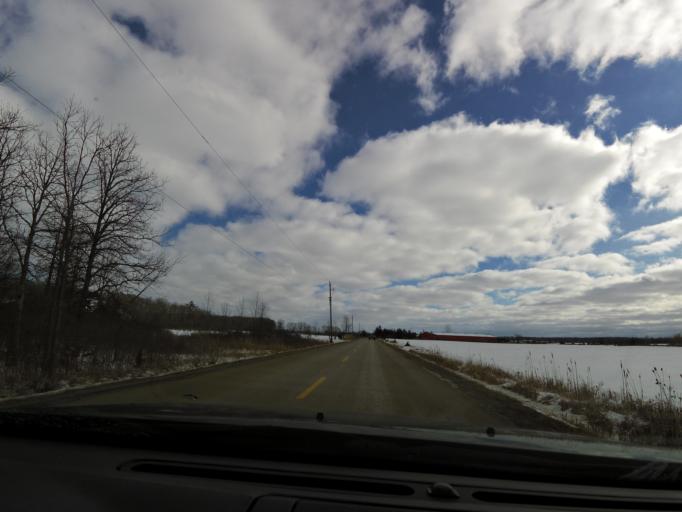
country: CA
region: Ontario
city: Hamilton
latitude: 43.1087
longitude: -79.6340
